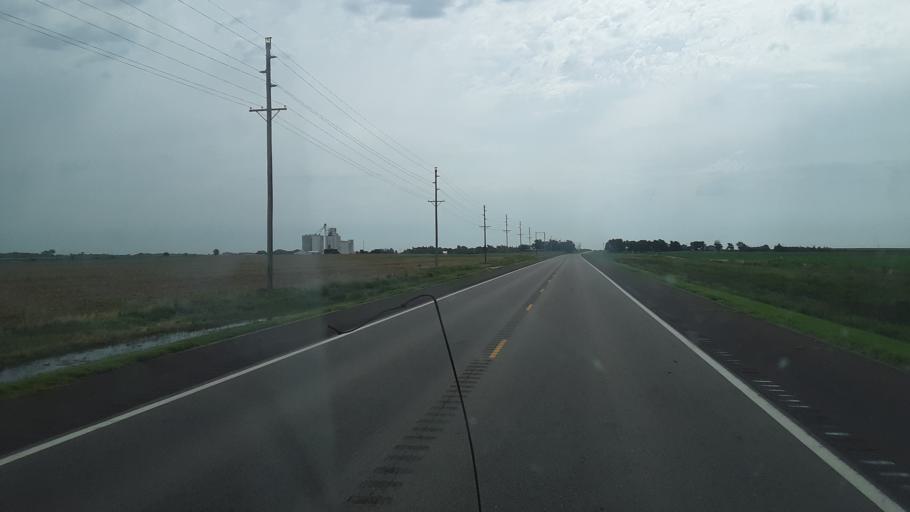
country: US
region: Kansas
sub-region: Stafford County
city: Stafford
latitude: 37.9550
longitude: -98.5089
